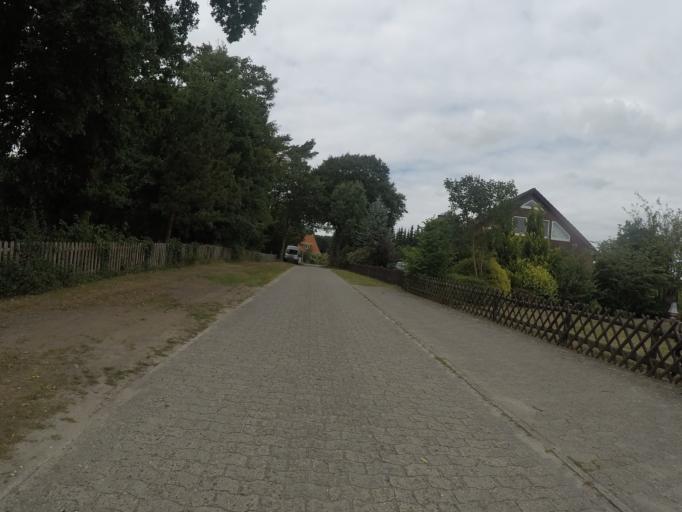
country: DE
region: Lower Saxony
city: Wingst
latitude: 53.7113
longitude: 9.0675
